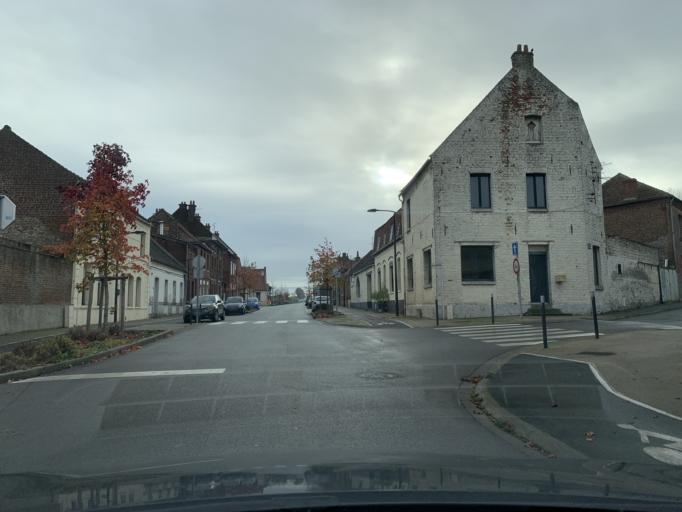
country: FR
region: Nord-Pas-de-Calais
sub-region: Departement du Nord
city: Cantin
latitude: 50.3091
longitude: 3.1279
